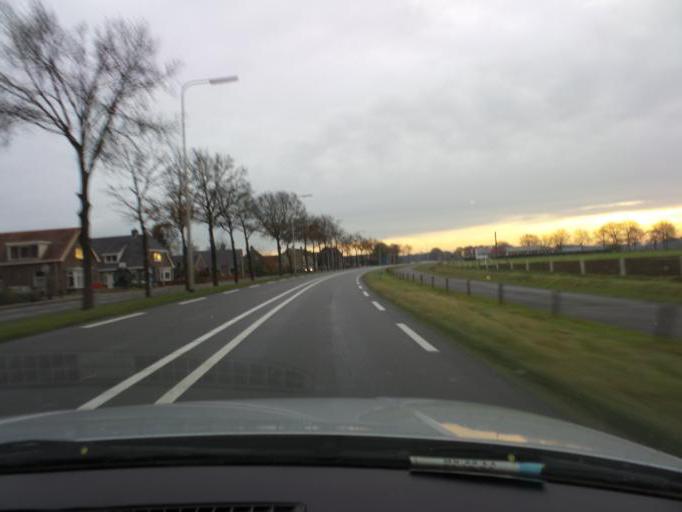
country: NL
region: Overijssel
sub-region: Gemeente Dalfsen
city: Dalfsen
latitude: 52.5318
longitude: 6.3130
